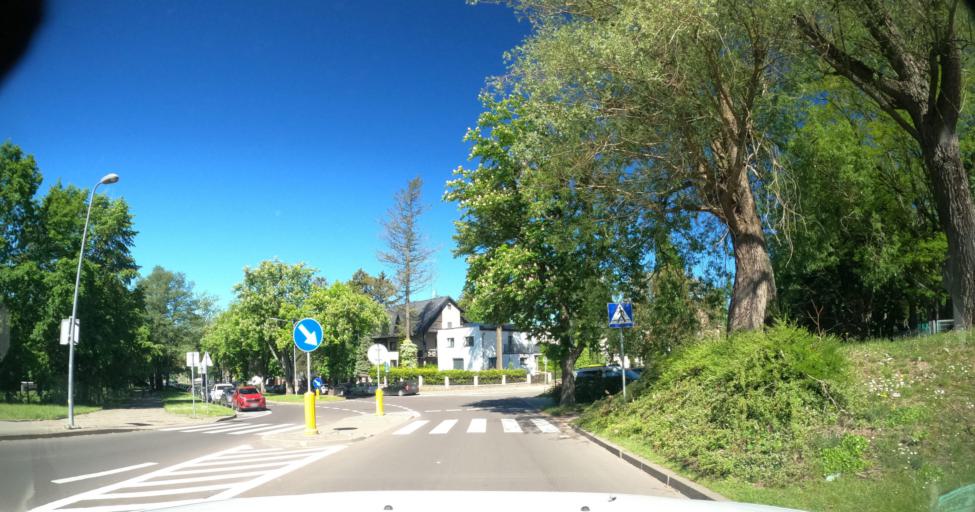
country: PL
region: Pomeranian Voivodeship
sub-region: Slupsk
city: Slupsk
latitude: 54.4737
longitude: 17.0421
